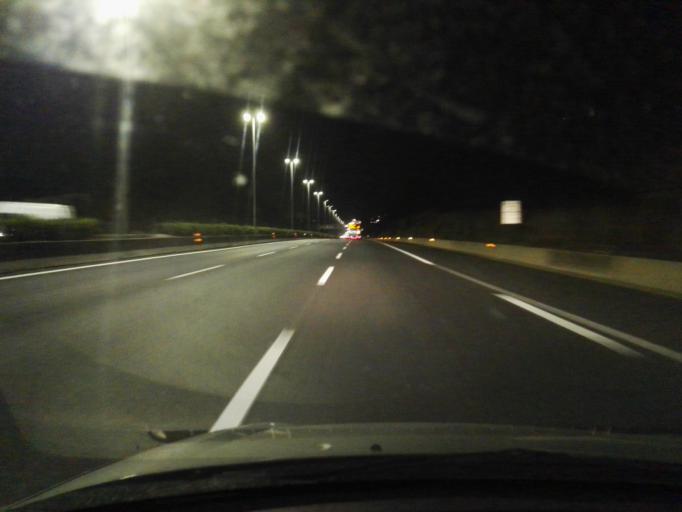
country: IT
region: Latium
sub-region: Citta metropolitana di Roma Capitale
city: Selcetta
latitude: 41.7985
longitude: 12.4745
